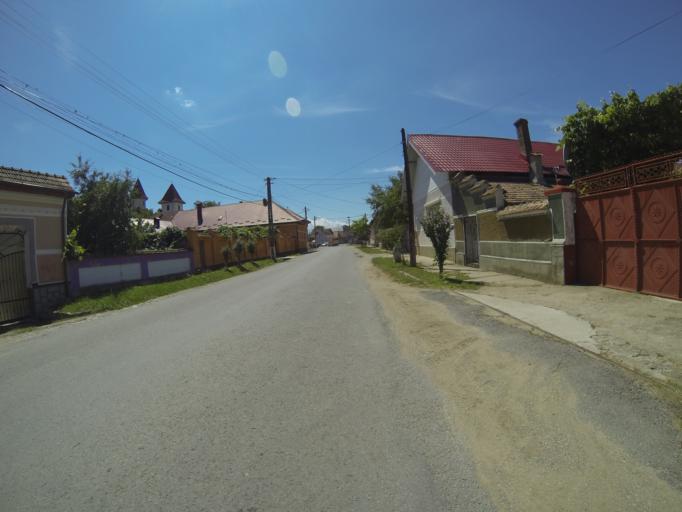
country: RO
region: Brasov
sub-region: Comuna Sinca Veche
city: Sinca Veche
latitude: 45.7640
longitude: 25.1685
